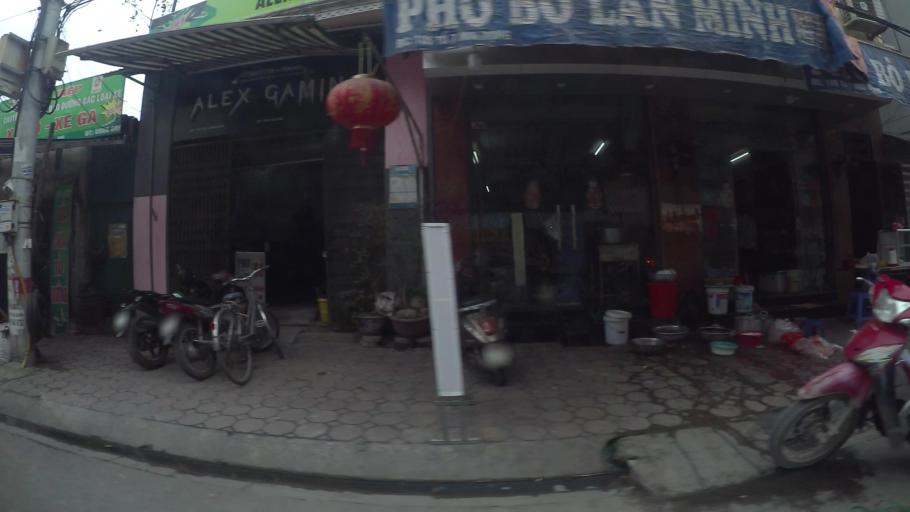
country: VN
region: Ha Noi
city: Hai BaTrung
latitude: 20.9918
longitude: 105.8589
